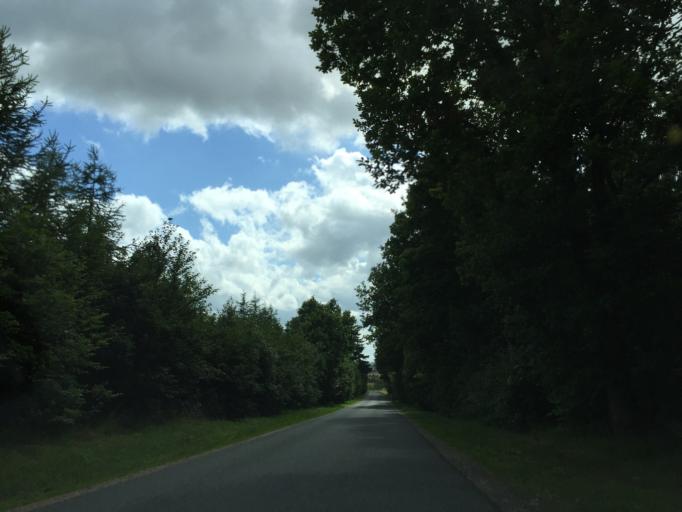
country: DK
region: Central Jutland
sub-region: Silkeborg Kommune
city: Svejbaek
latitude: 56.2022
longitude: 9.7078
